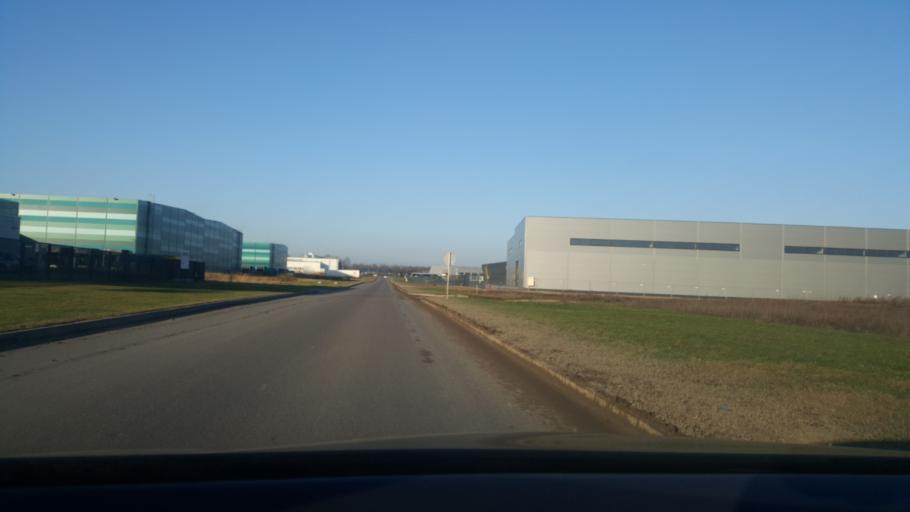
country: LT
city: Ramuciai
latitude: 54.9399
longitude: 24.0162
